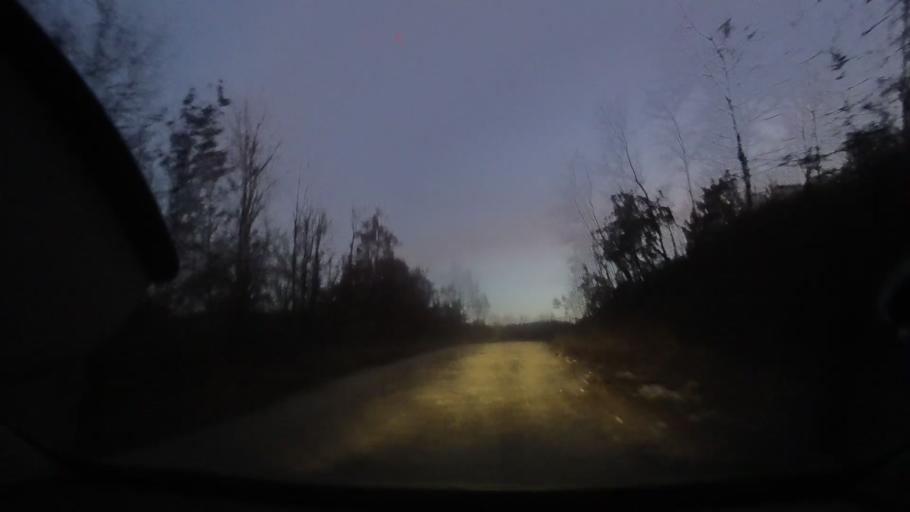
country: RO
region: Bihor
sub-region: Comuna Varciorog
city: Varciorog
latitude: 46.9952
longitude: 22.3080
